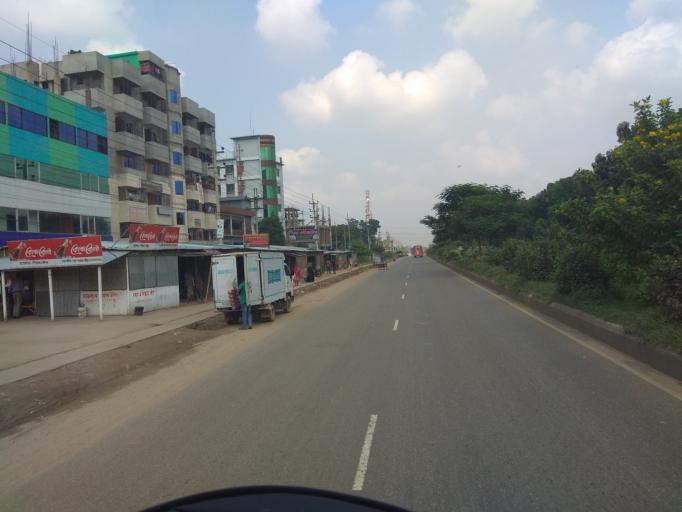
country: BD
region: Dhaka
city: Tungi
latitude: 24.1770
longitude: 90.4273
